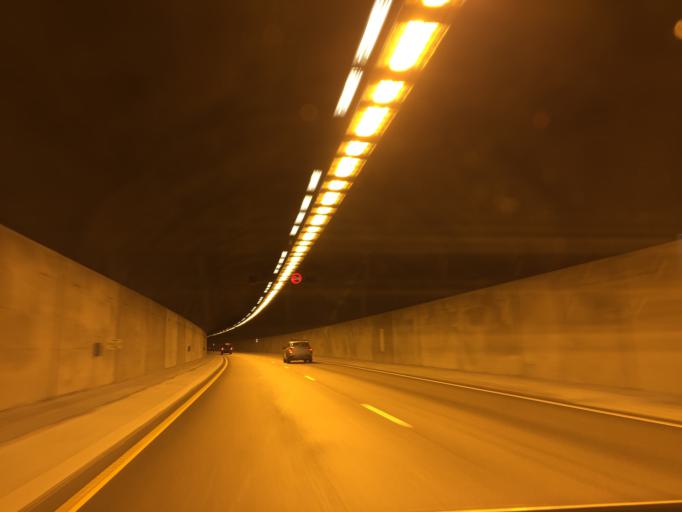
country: NO
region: Buskerud
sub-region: Lier
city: Tranby
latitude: 59.7955
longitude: 10.2681
